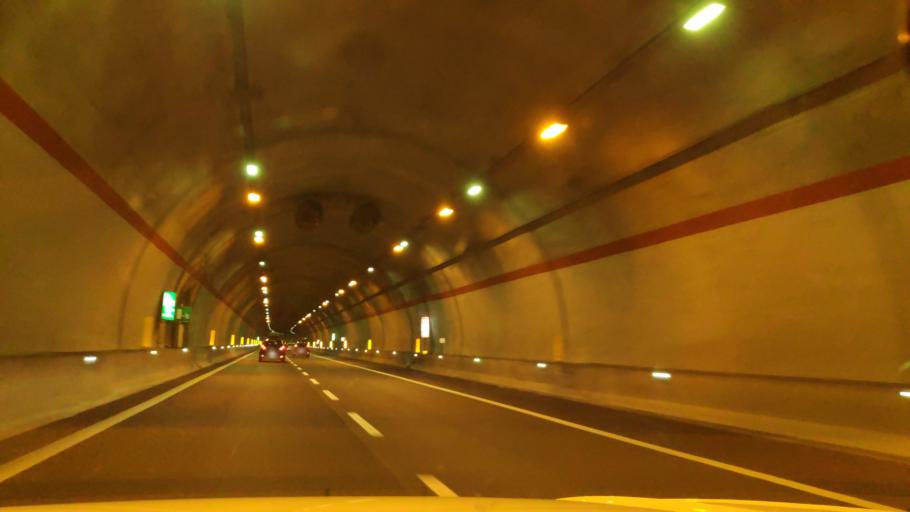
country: IT
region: Calabria
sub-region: Provincia di Cosenza
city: Morano Calabro
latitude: 39.8748
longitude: 16.1251
